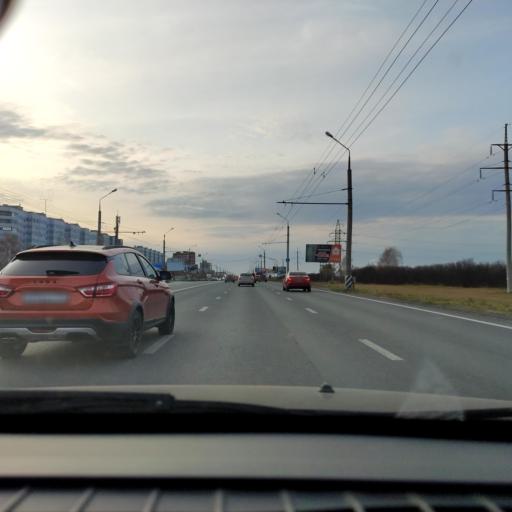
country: RU
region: Samara
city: Tol'yatti
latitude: 53.5473
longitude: 49.3568
